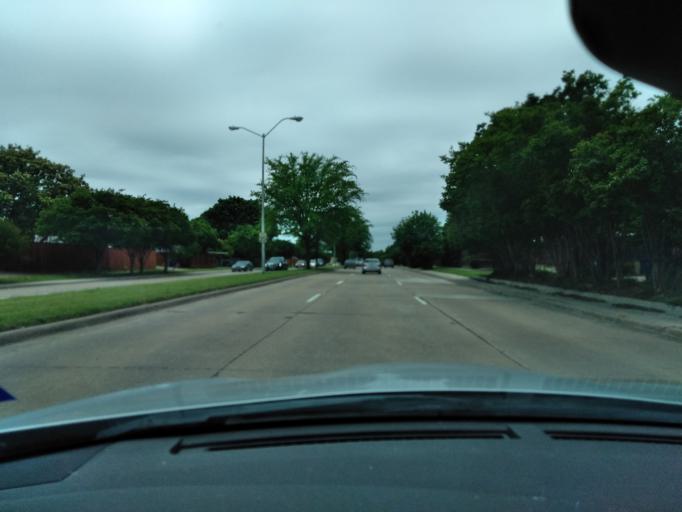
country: US
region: Texas
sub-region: Dallas County
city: Addison
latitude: 32.9703
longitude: -96.7845
